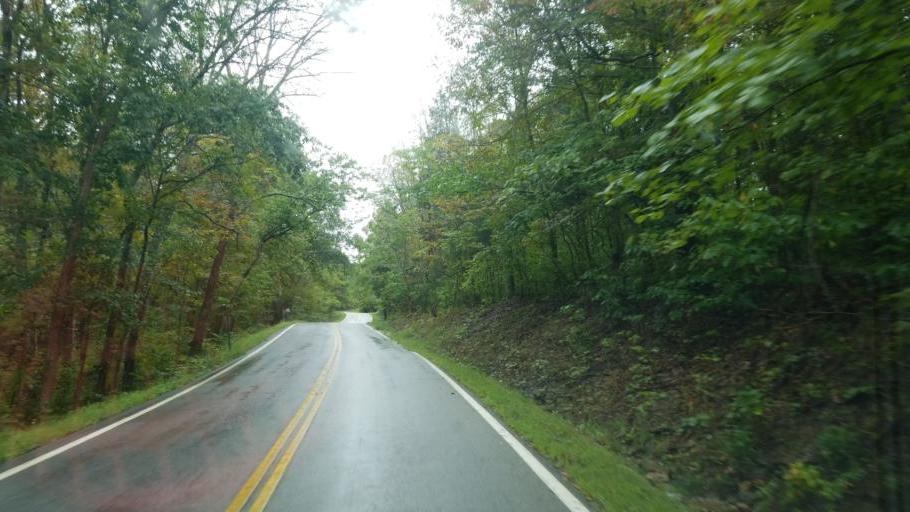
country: US
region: Ohio
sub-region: Adams County
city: West Union
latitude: 38.7428
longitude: -83.5180
